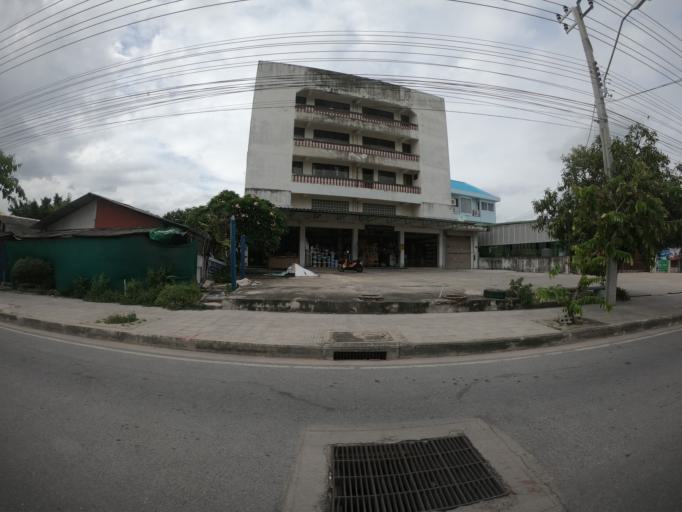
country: TH
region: Bangkok
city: Bang Na
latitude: 13.6823
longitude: 100.6716
